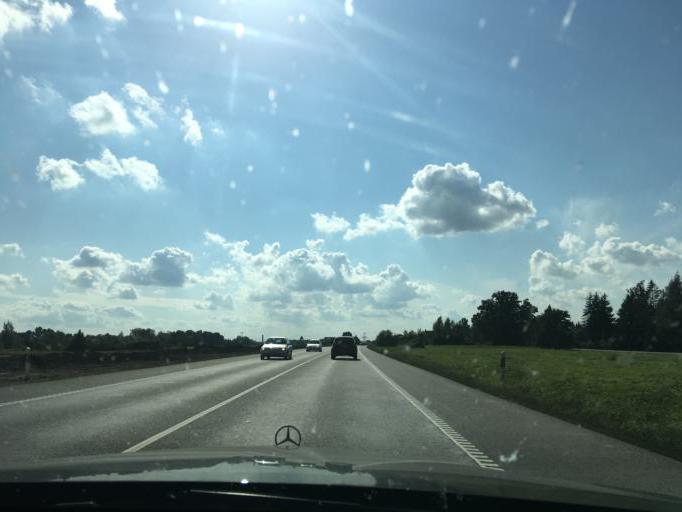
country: LT
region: Marijampoles apskritis
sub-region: Marijampole Municipality
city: Marijampole
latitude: 54.6048
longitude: 23.4064
